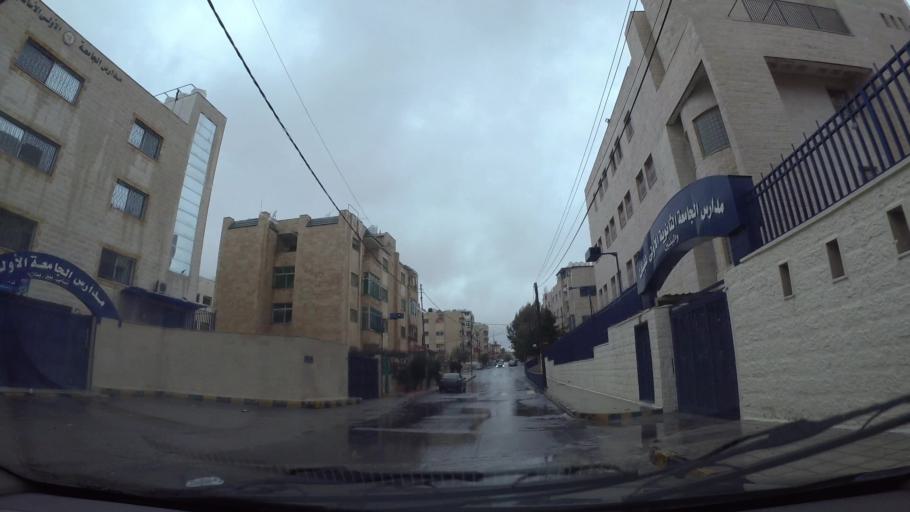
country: JO
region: Amman
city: Al Jubayhah
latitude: 32.0243
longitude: 35.8750
